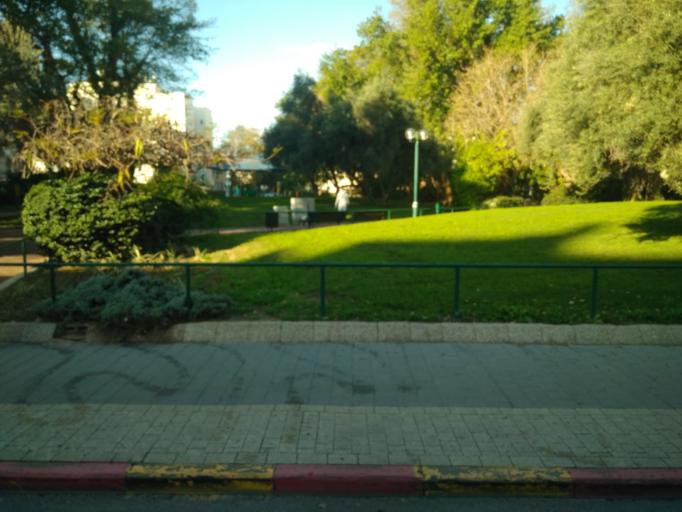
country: IL
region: Tel Aviv
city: Tel Aviv
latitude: 32.0956
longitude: 34.7940
